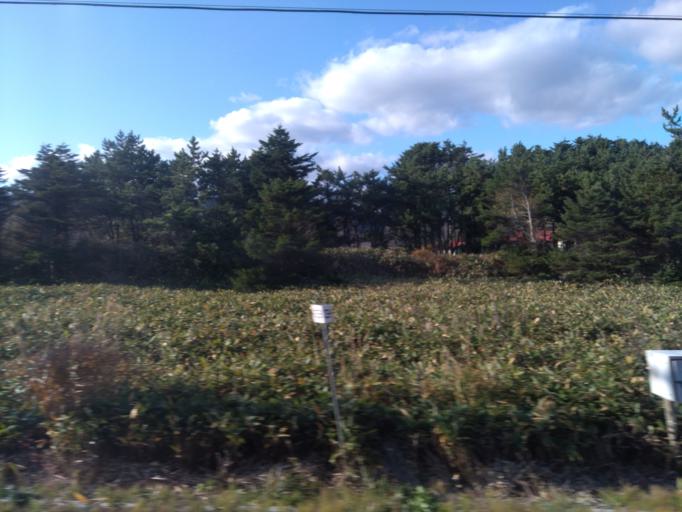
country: JP
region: Hokkaido
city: Niseko Town
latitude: 42.5759
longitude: 140.4492
